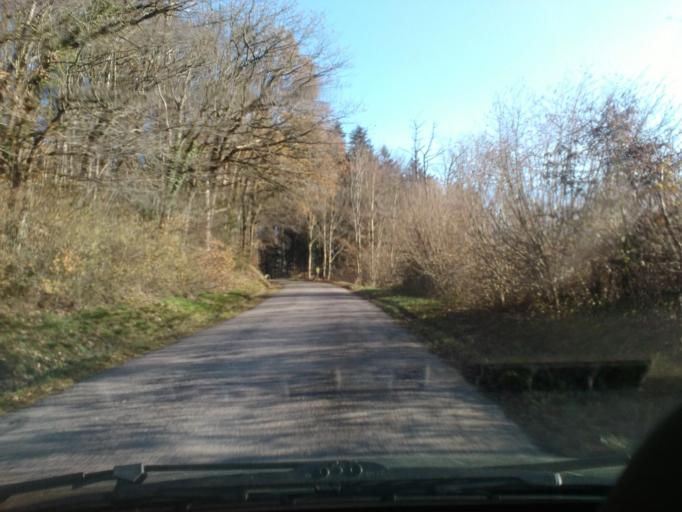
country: FR
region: Lorraine
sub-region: Departement des Vosges
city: Senones
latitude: 48.3459
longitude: 6.9658
